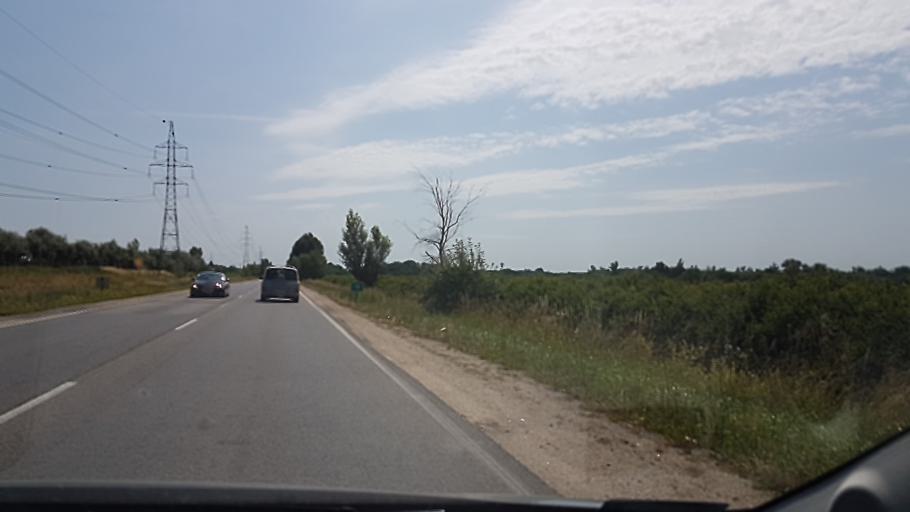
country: HU
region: Pest
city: Dunaharaszti
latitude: 47.3408
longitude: 19.1132
